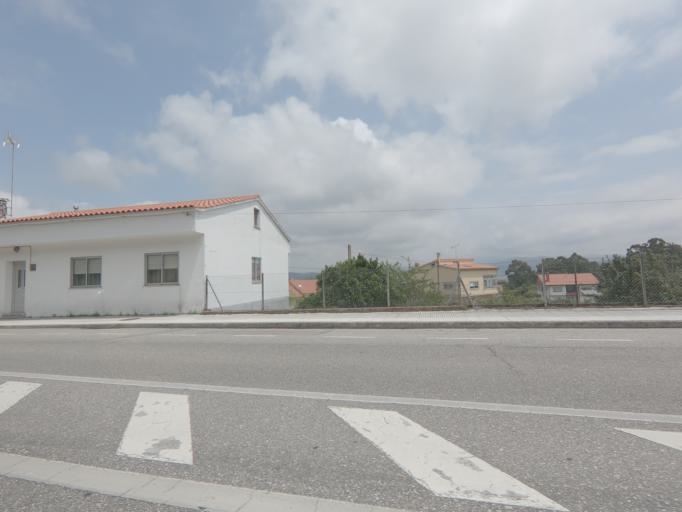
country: ES
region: Galicia
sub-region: Provincia de Pontevedra
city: A Guarda
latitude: 41.9025
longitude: -8.8643
